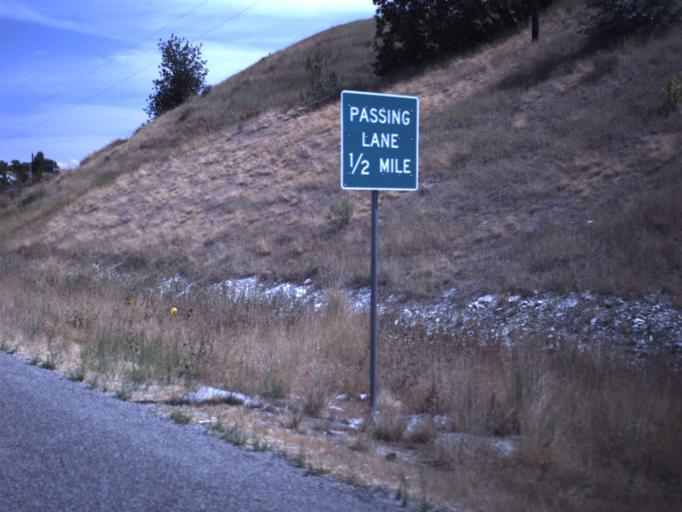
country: US
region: Utah
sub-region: Cache County
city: Mendon
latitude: 41.7967
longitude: -112.0459
